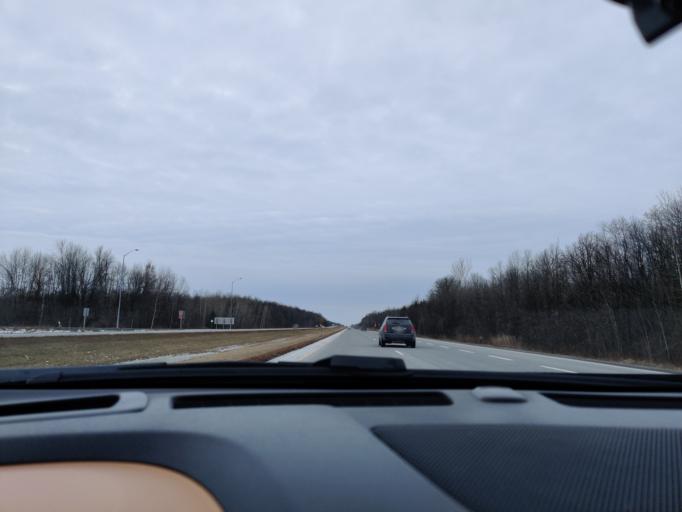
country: US
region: New York
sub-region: St. Lawrence County
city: Ogdensburg
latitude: 44.8569
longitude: -75.3316
